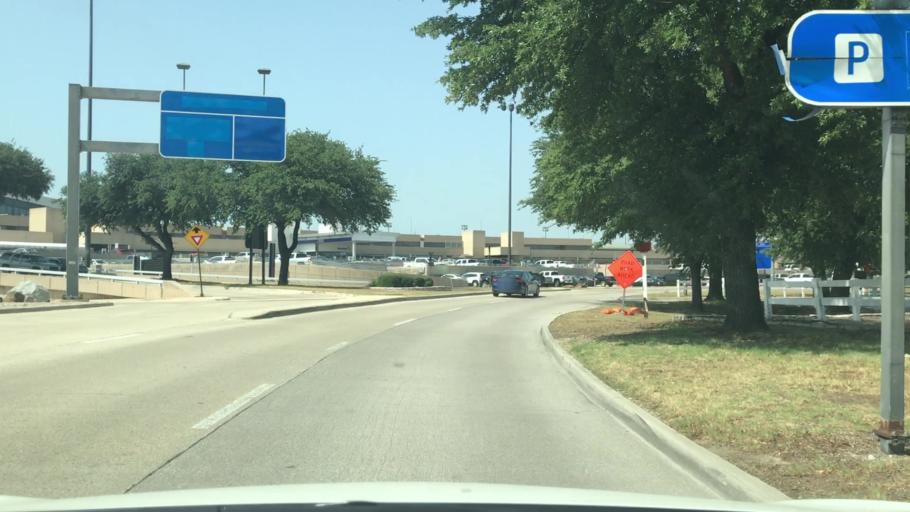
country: US
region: Texas
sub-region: Tarrant County
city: Grapevine
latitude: 32.9049
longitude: -97.0435
